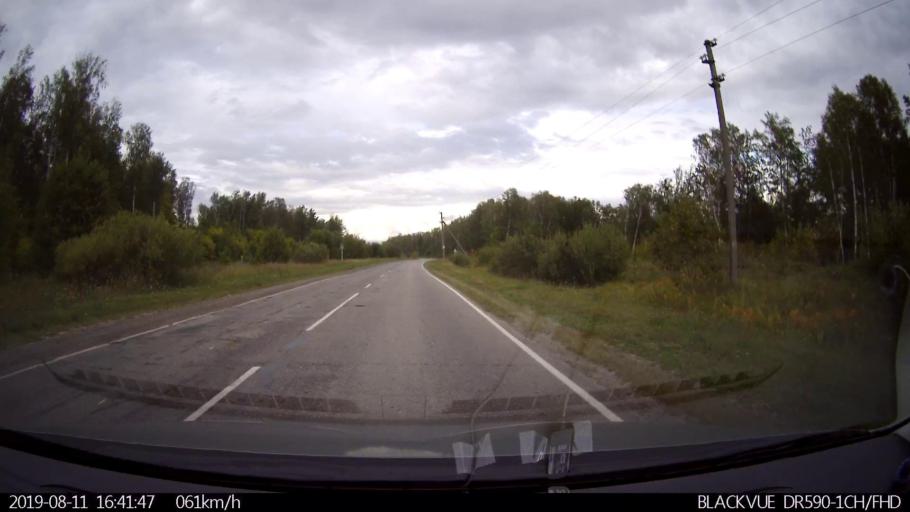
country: RU
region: Ulyanovsk
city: Mayna
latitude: 54.1557
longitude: 47.6561
